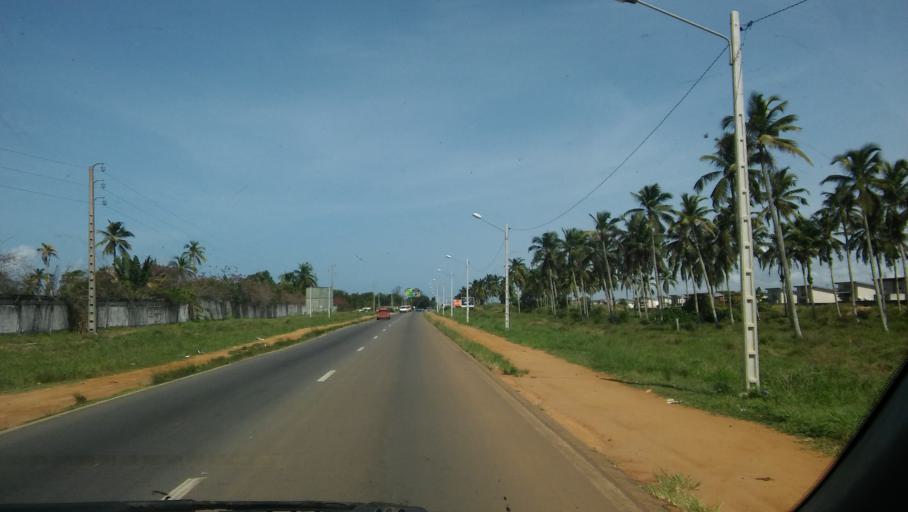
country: CI
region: Sud-Comoe
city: Grand-Bassam
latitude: 5.2116
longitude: -3.7743
